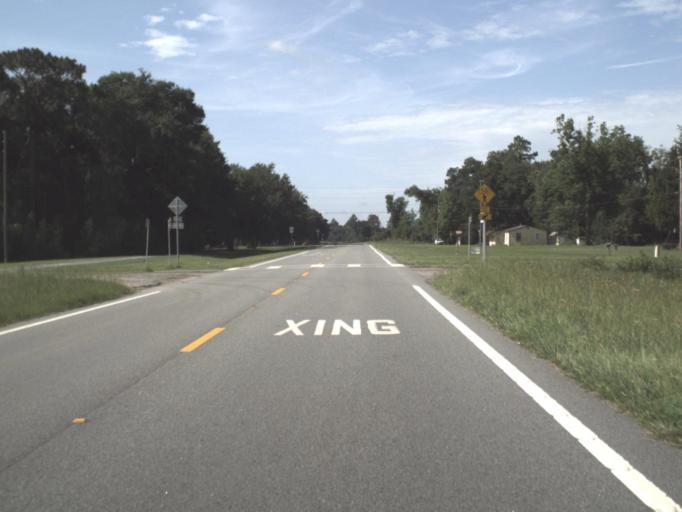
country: US
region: Florida
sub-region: Madison County
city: Madison
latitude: 30.5532
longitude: -83.3673
